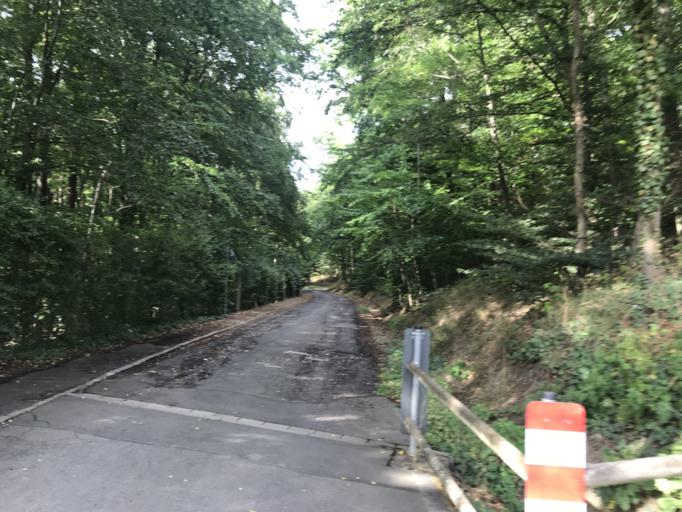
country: DE
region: Hesse
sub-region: Regierungsbezirk Giessen
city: Lohra
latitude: 50.6683
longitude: 8.6046
